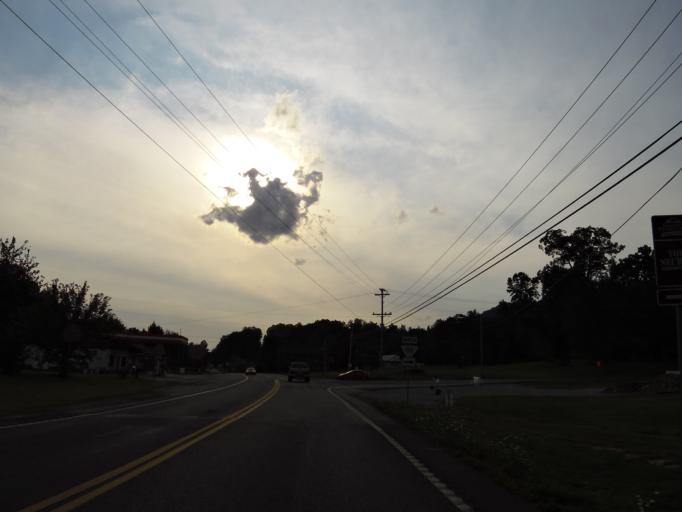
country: US
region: Tennessee
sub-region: Morgan County
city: Coalfield
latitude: 36.0700
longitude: -84.4613
